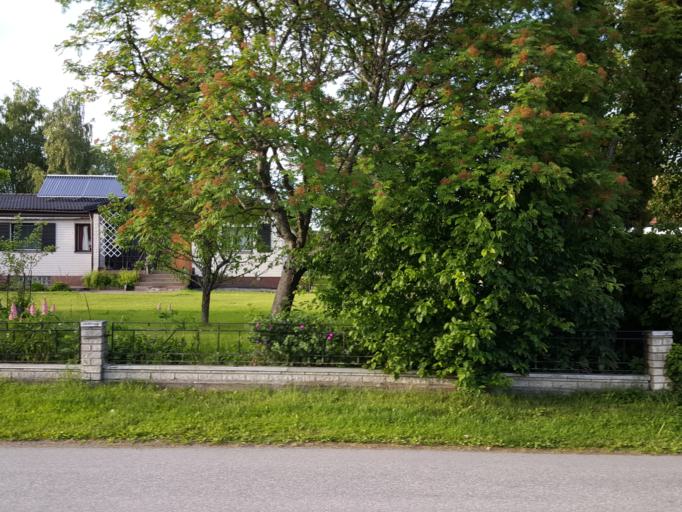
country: SE
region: Uppsala
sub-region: Osthammars Kommun
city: Gimo
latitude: 60.1689
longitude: 18.1888
